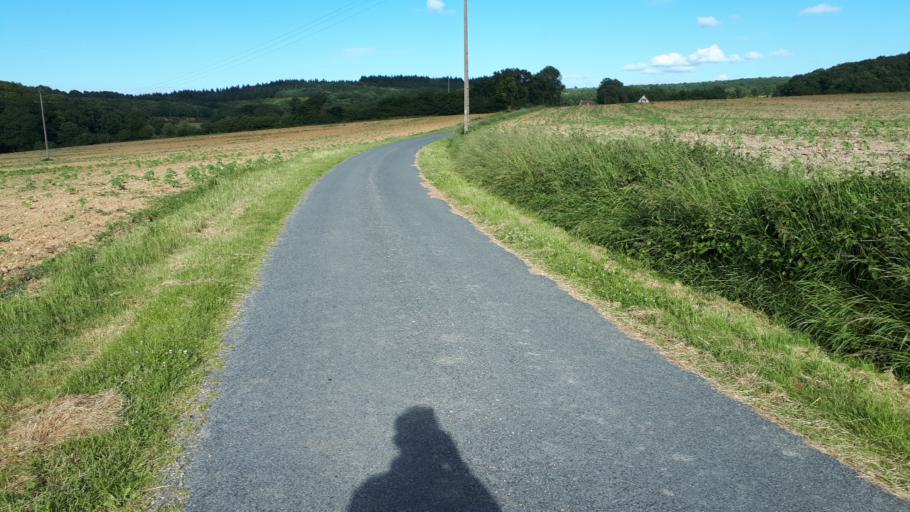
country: FR
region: Centre
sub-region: Departement du Loir-et-Cher
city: Sarge-sur-Braye
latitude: 47.9277
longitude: 0.8623
